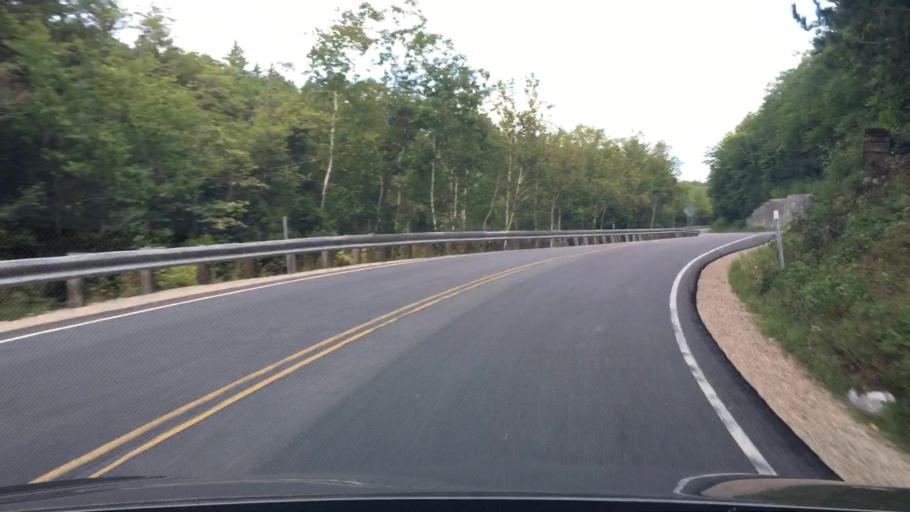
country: US
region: New Hampshire
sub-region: Carroll County
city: Conway
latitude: 43.9934
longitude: -71.2103
